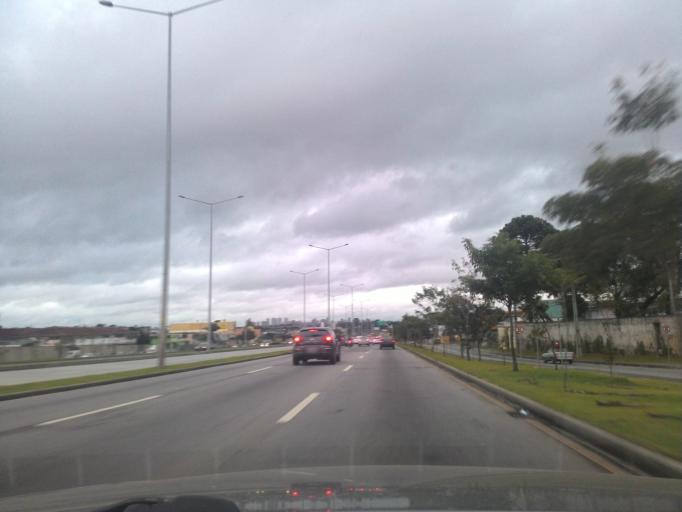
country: BR
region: Parana
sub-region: Curitiba
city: Curitiba
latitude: -25.4799
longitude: -49.2624
